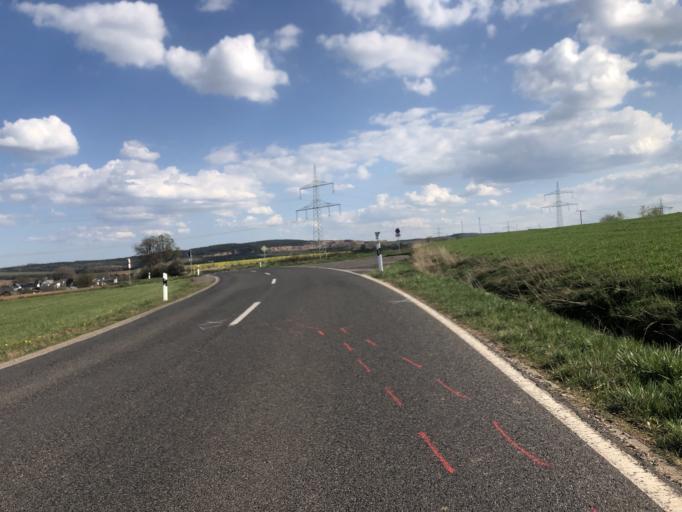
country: DE
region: North Rhine-Westphalia
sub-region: Regierungsbezirk Koln
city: Kall
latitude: 50.5878
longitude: 6.5763
